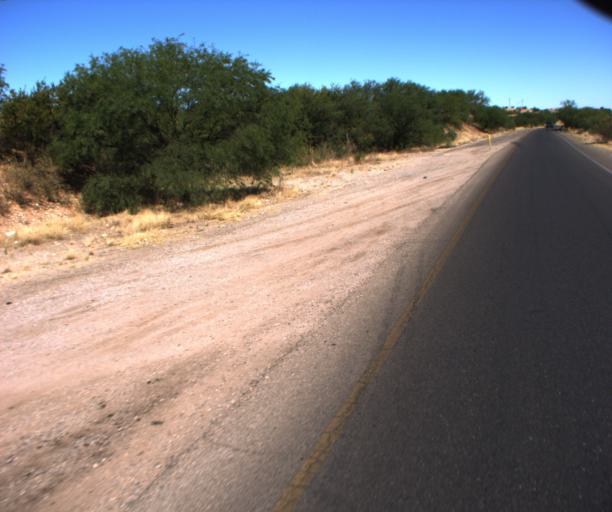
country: US
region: Arizona
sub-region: Santa Cruz County
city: Nogales
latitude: 31.3949
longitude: -110.9572
